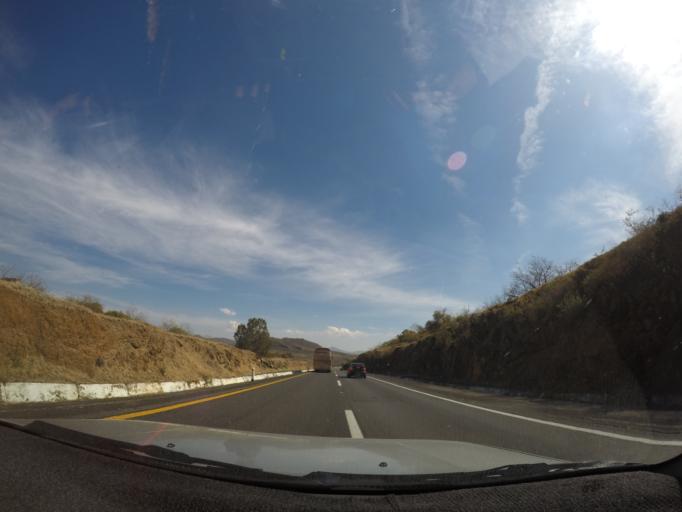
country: MX
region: Veracruz
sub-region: Papantla
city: Polutla
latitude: 20.4787
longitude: -97.2621
